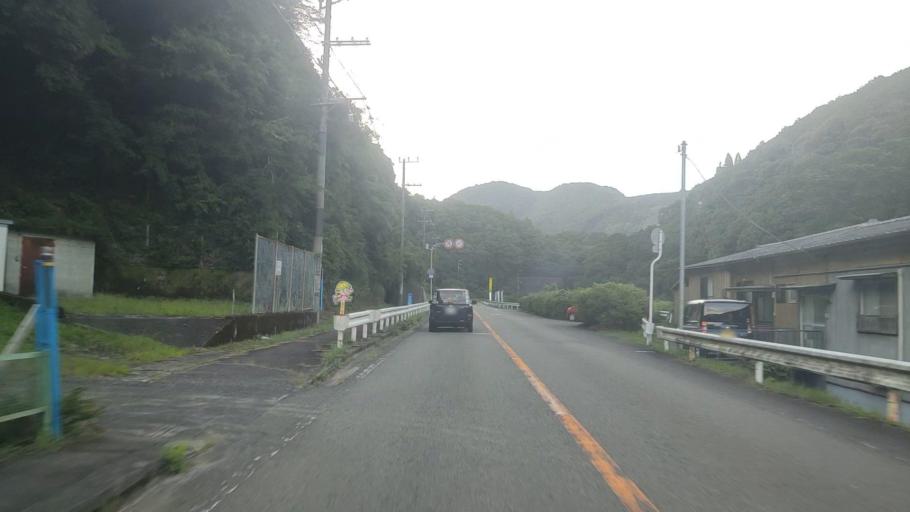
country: JP
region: Wakayama
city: Tanabe
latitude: 33.7962
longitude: 135.5191
